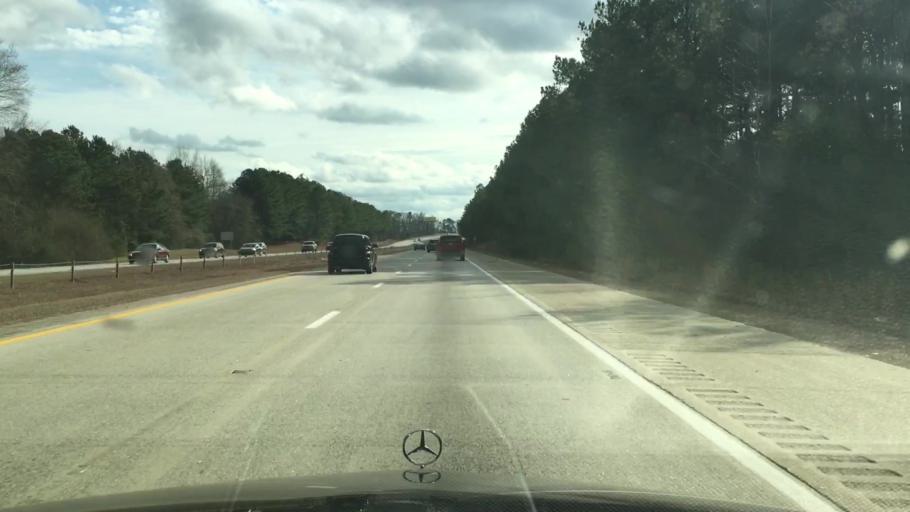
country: US
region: North Carolina
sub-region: Johnston County
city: Benson
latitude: 35.4171
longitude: -78.5274
